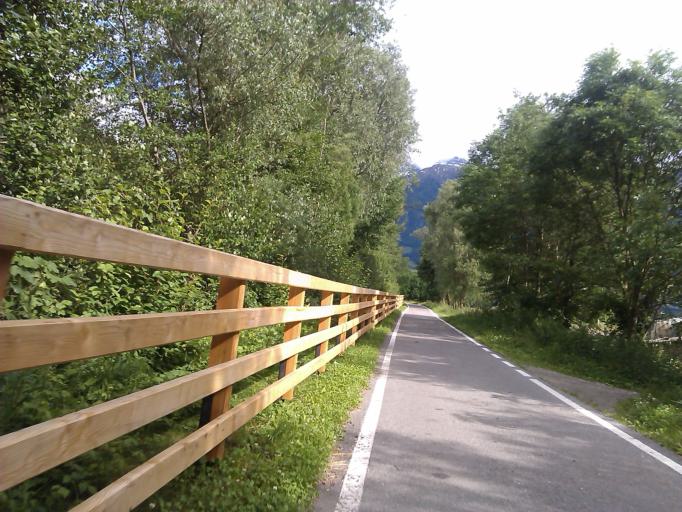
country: IT
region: Trentino-Alto Adige
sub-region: Bolzano
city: Sluderno
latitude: 46.6487
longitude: 10.5758
